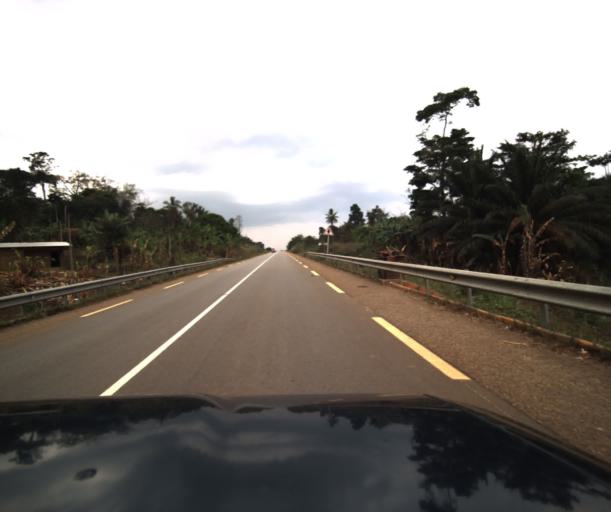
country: CM
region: Centre
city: Akono
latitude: 3.6363
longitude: 11.3264
